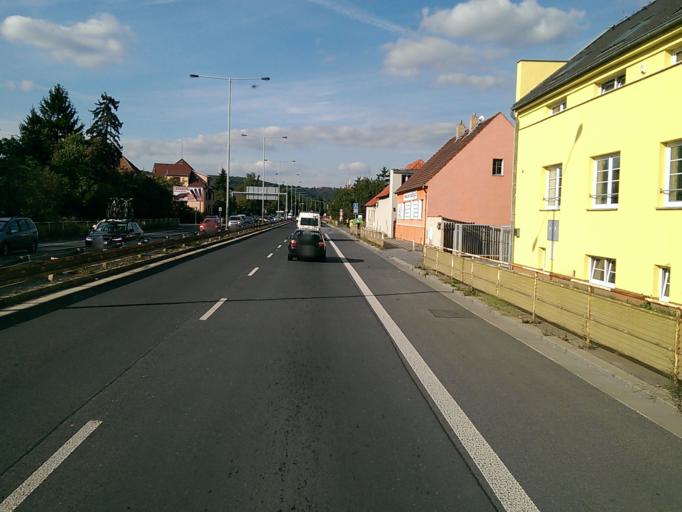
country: CZ
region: Praha
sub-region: Praha 12
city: Modrany
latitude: 49.9994
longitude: 14.3961
